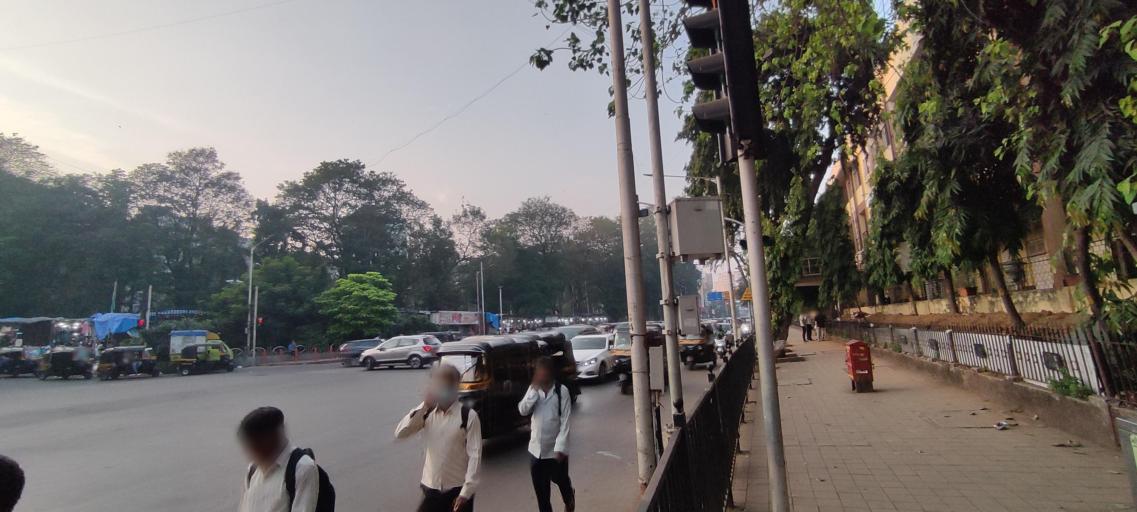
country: IN
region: Maharashtra
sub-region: Mumbai Suburban
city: Mumbai
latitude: 19.0637
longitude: 72.8352
